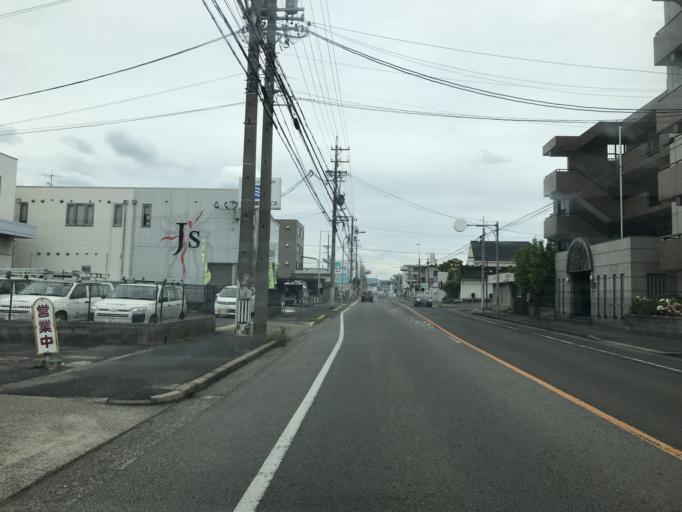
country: JP
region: Aichi
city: Kasugai
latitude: 35.2598
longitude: 136.9774
